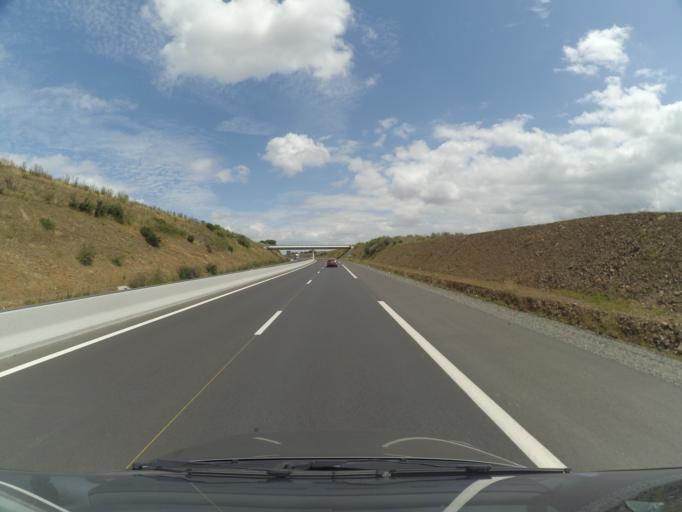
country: FR
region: Brittany
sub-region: Departement des Cotes-d'Armor
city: Langueux
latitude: 48.4769
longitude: -2.7106
